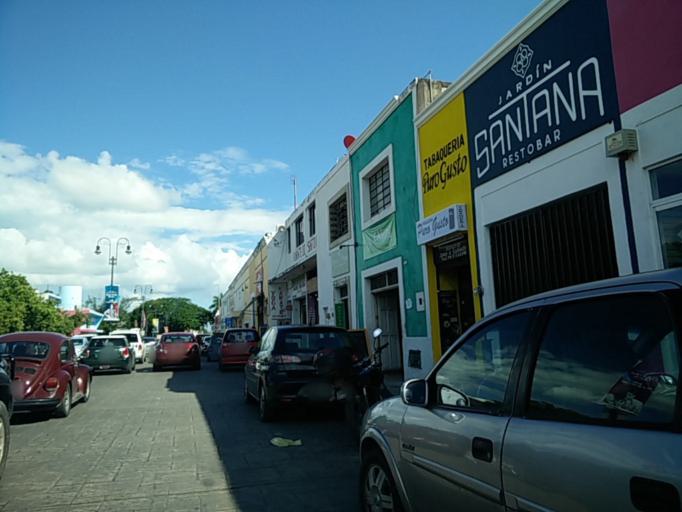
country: MX
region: Yucatan
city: Merida
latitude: 20.9755
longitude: -89.6212
